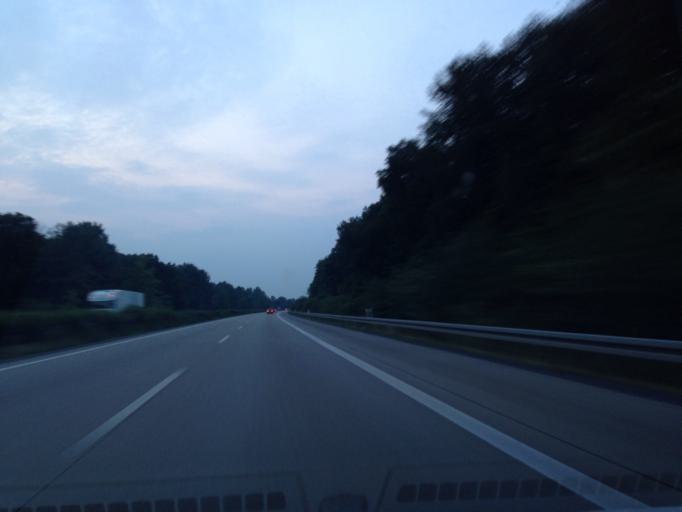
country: DE
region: North Rhine-Westphalia
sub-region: Regierungsbezirk Munster
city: Senden
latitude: 51.8549
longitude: 7.5782
